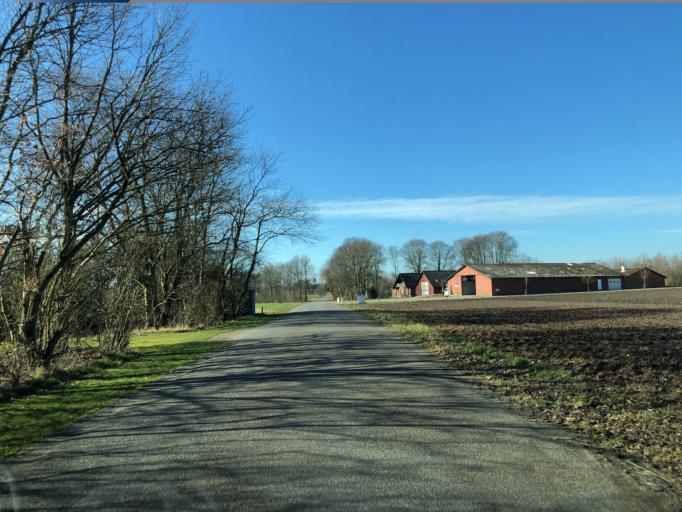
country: DK
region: Central Jutland
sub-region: Ikast-Brande Kommune
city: Bording Kirkeby
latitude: 56.1553
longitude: 9.2433
